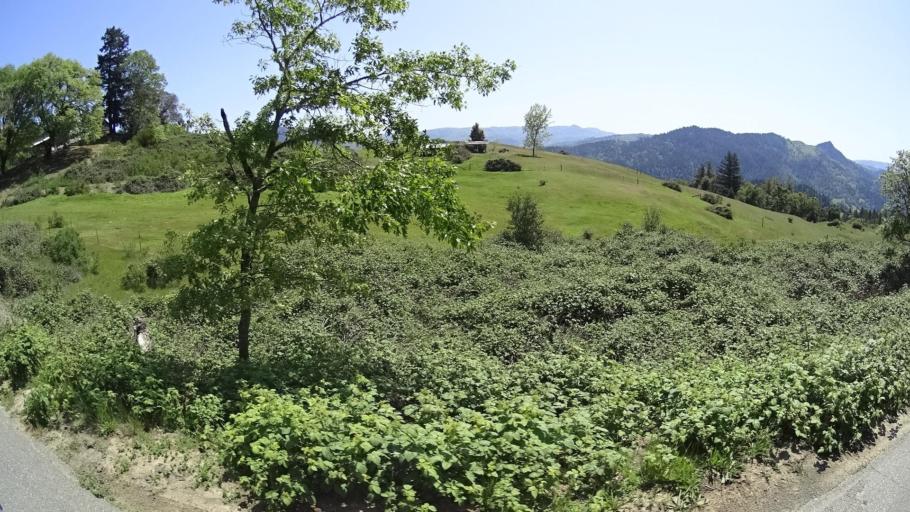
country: US
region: California
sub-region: Humboldt County
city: Redway
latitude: 40.1335
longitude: -123.6287
